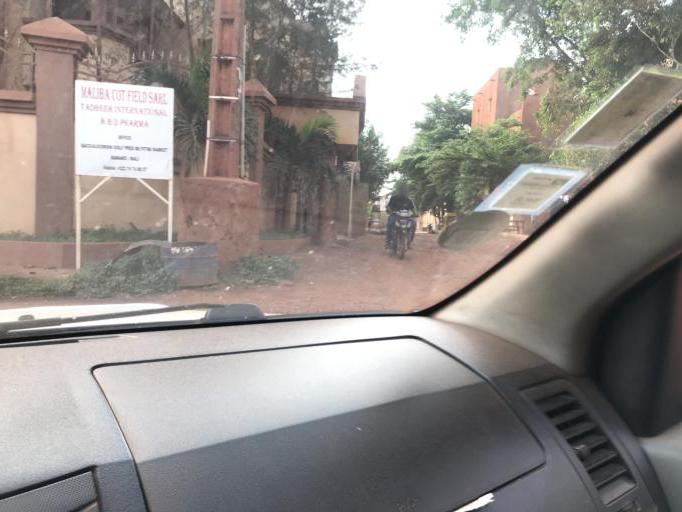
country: ML
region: Bamako
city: Bamako
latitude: 12.5818
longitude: -8.0028
